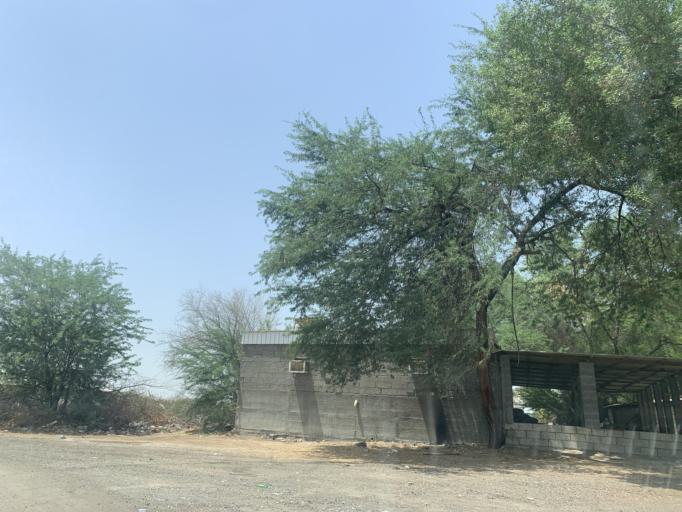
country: BH
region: Central Governorate
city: Madinat Hamad
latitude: 26.1560
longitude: 50.4931
